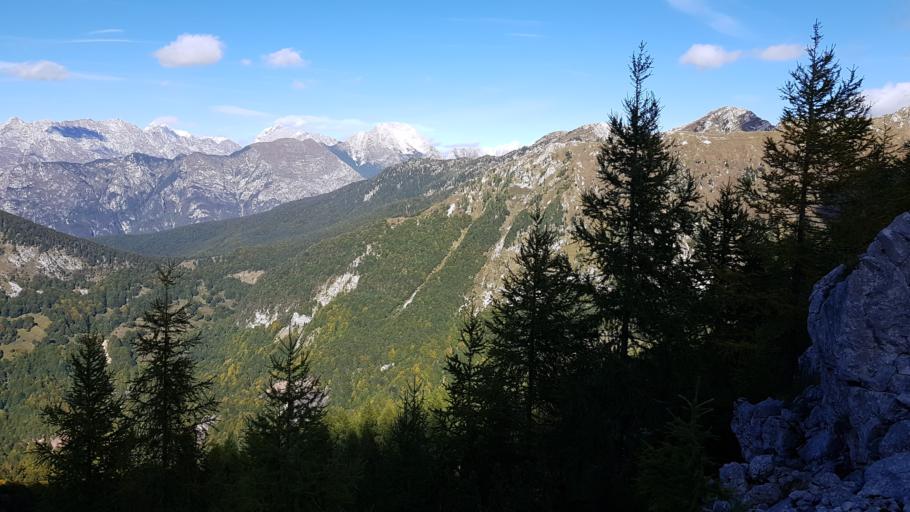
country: SI
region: Kobarid
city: Kobarid
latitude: 46.2914
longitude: 13.6021
